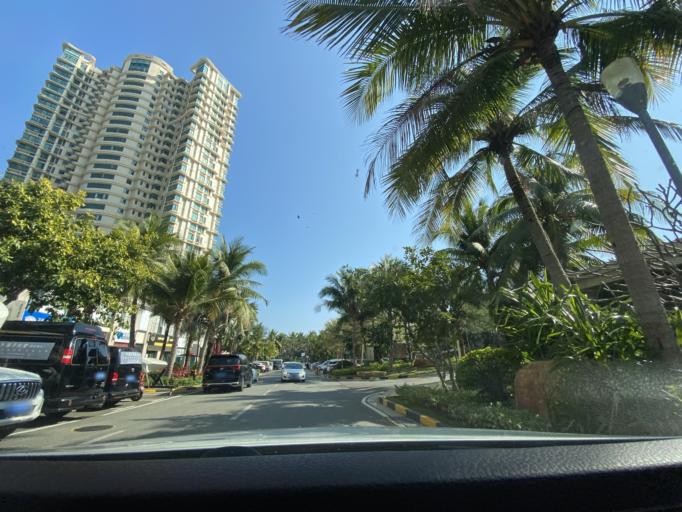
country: CN
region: Hainan
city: Yingzhou
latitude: 18.4095
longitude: 109.8750
